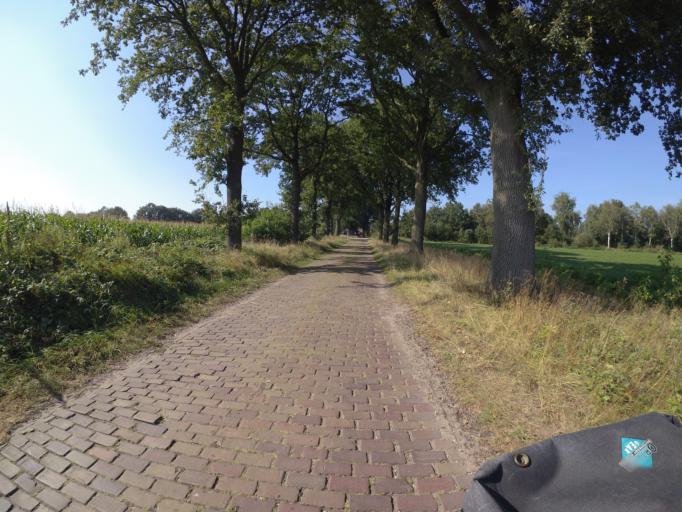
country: NL
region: North Brabant
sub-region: Gemeente Uden
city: Odiliapeel
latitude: 51.6689
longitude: 5.7110
